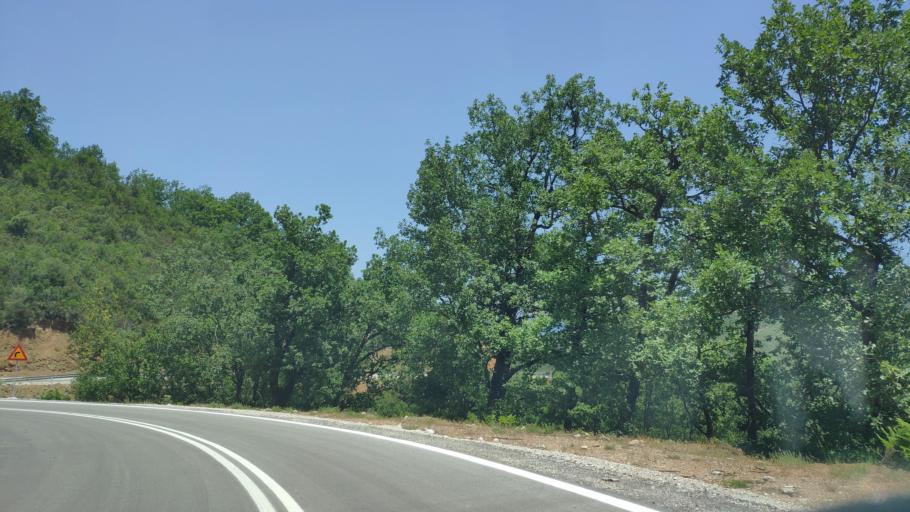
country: GR
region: Epirus
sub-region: Nomos Artas
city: Ano Kalentini
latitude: 39.1837
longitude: 21.3578
